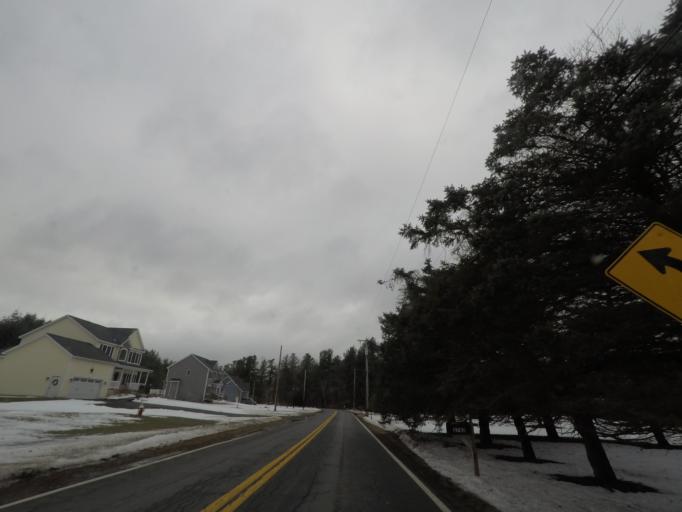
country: US
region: New York
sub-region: Schenectady County
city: Rotterdam
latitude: 42.7472
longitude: -73.9632
